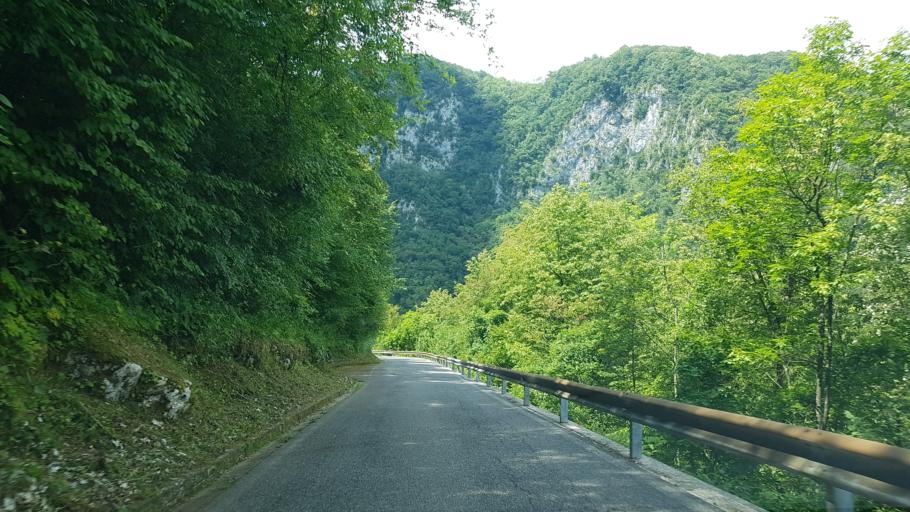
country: IT
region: Friuli Venezia Giulia
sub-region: Provincia di Udine
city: Lusevera
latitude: 46.2506
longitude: 13.2546
